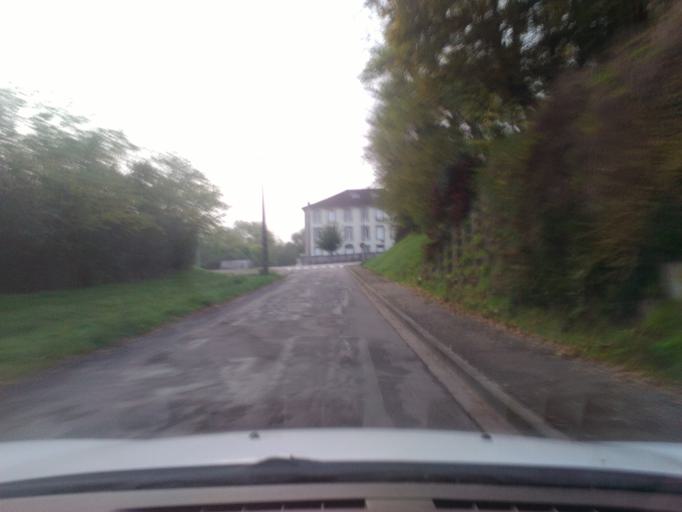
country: FR
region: Lorraine
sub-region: Departement des Vosges
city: Mirecourt
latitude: 48.2994
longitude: 6.1283
